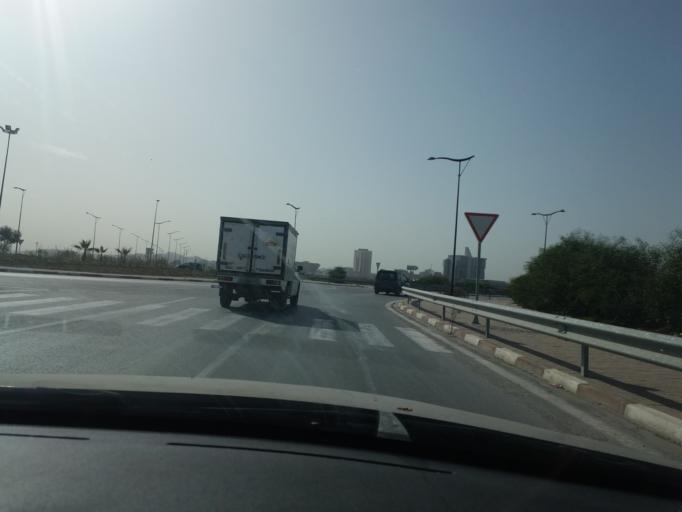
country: TN
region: Tunis
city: Tunis
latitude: 36.8136
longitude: 10.1943
